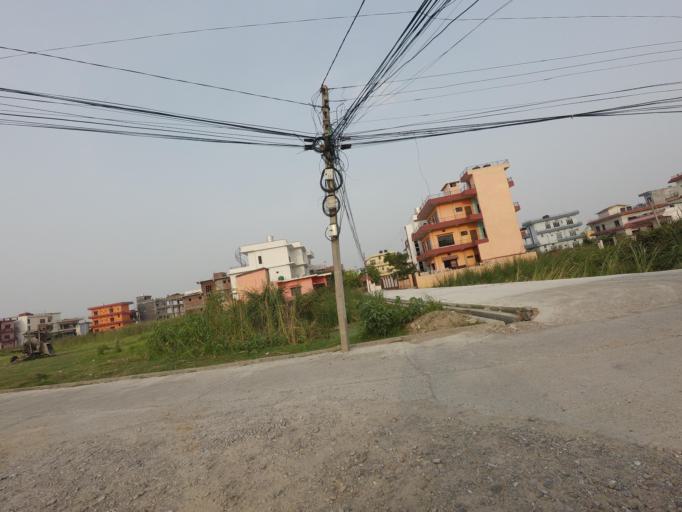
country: NP
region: Western Region
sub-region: Lumbini Zone
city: Bhairahawa
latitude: 27.5130
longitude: 83.4591
